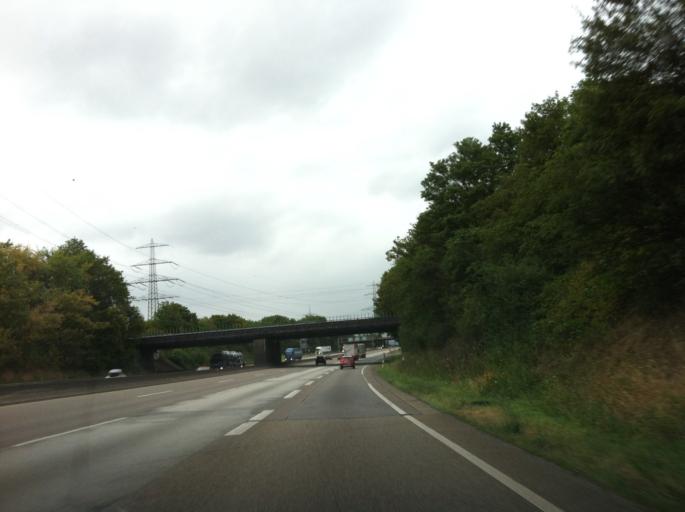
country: DE
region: Hesse
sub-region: Regierungsbezirk Darmstadt
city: Eschborn
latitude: 50.1307
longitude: 8.5903
